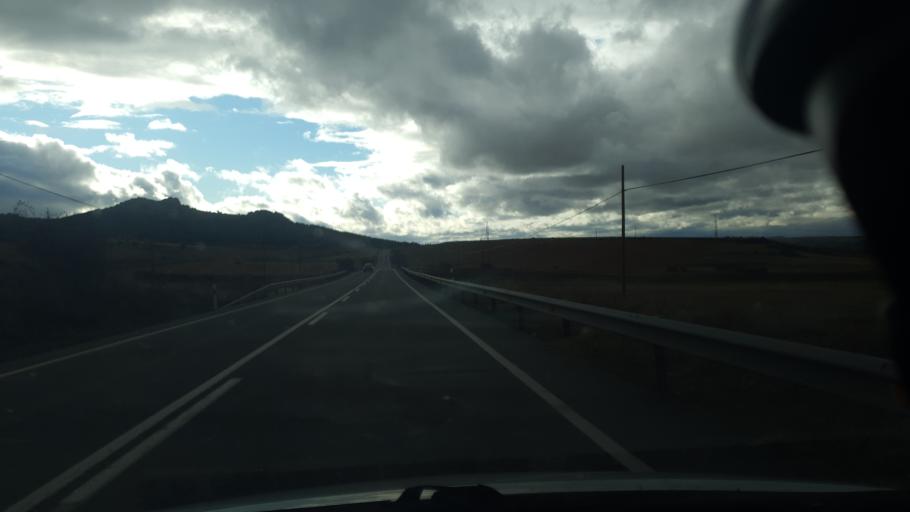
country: ES
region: Castille and Leon
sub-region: Provincia de Avila
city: Ojos-Albos
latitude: 40.7389
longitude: -4.4812
